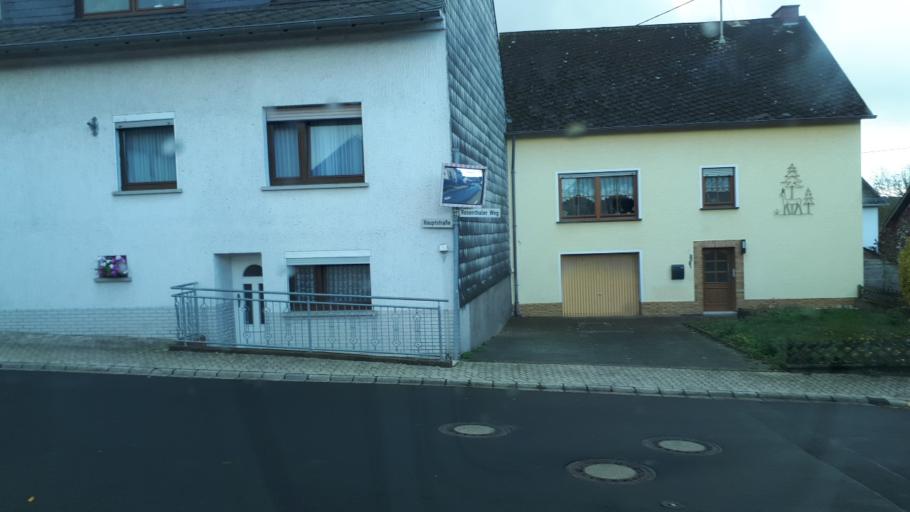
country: DE
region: Rheinland-Pfalz
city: Binningen
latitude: 50.2052
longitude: 7.2414
